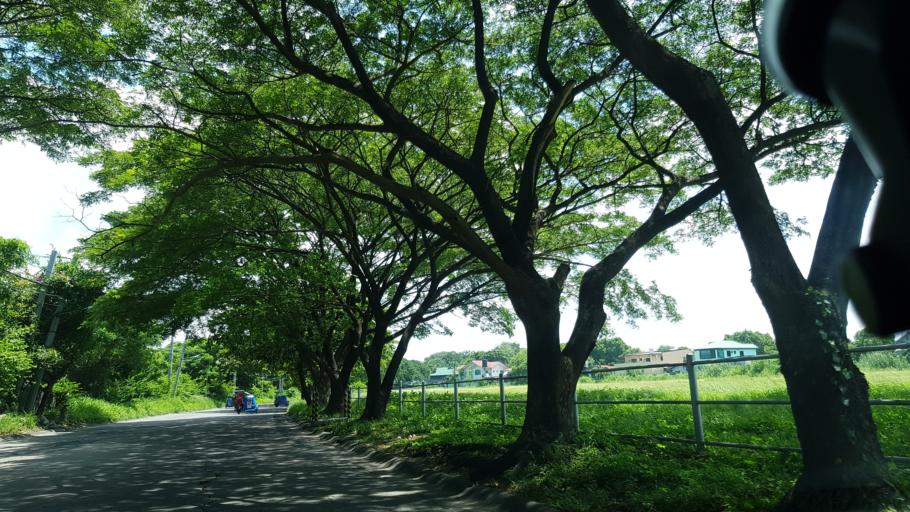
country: PH
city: Sambayanihan People's Village
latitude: 14.4468
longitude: 121.0107
